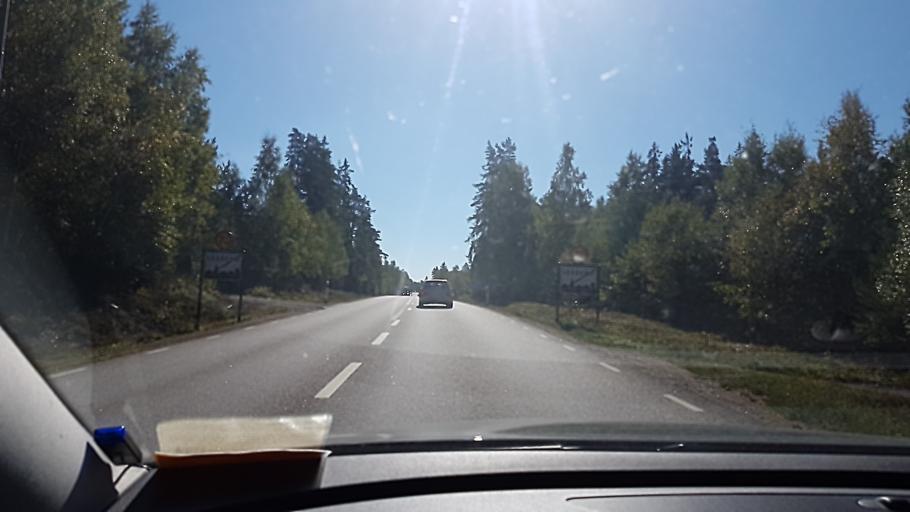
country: SE
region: Kronoberg
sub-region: Lessebo Kommun
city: Lessebo
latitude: 56.7432
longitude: 15.2704
